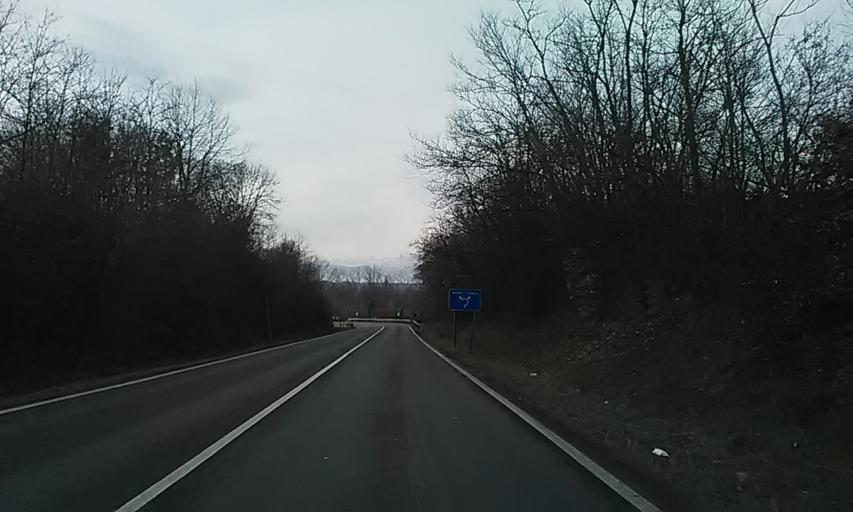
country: IT
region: Piedmont
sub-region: Provincia di Torino
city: Rondissone
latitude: 45.2716
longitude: 7.9815
